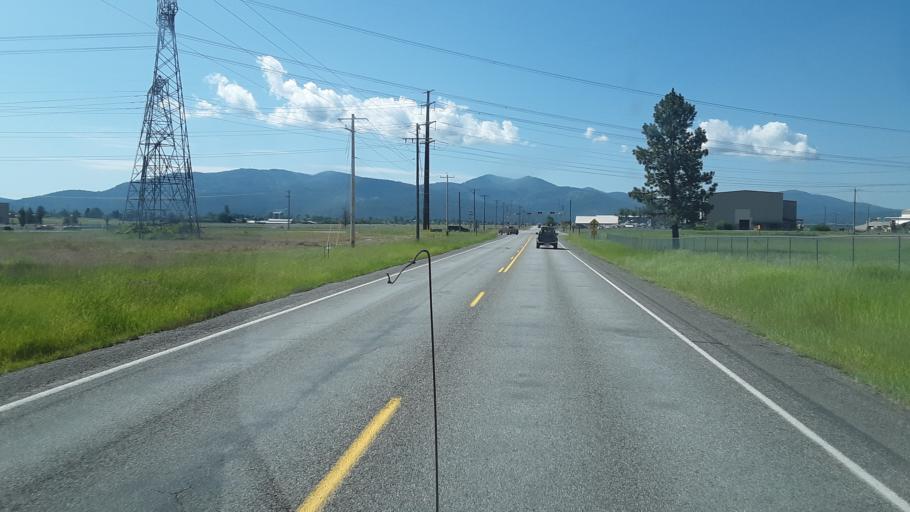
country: US
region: Idaho
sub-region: Kootenai County
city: Post Falls
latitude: 47.7470
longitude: -117.0020
